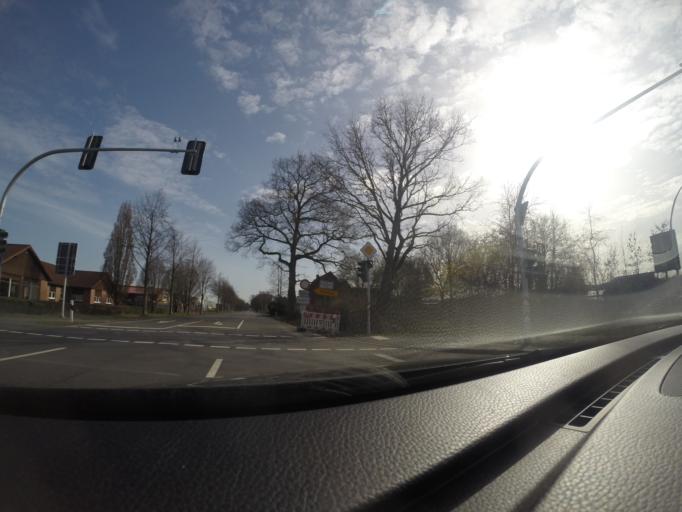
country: DE
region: North Rhine-Westphalia
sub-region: Regierungsbezirk Munster
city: Legden
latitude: 52.0408
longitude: 7.0893
